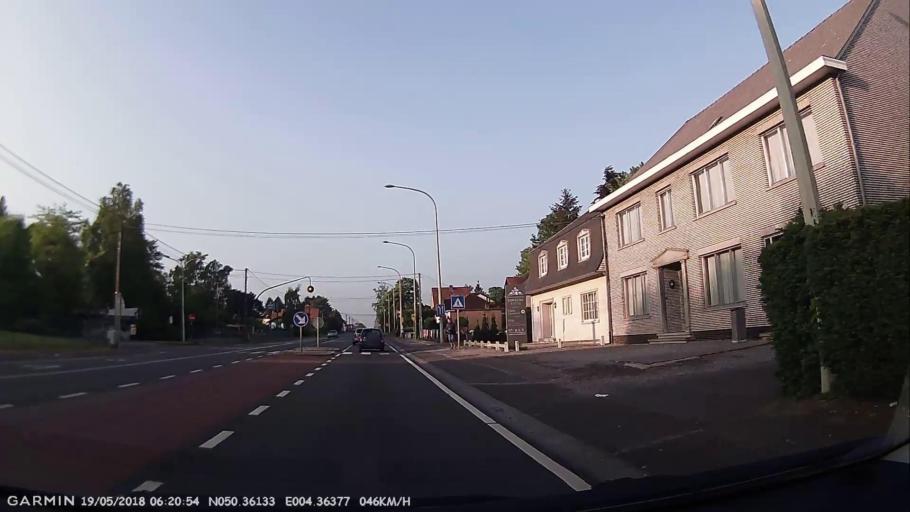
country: BE
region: Wallonia
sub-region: Province du Hainaut
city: Thuin
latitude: 50.3613
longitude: 4.3638
